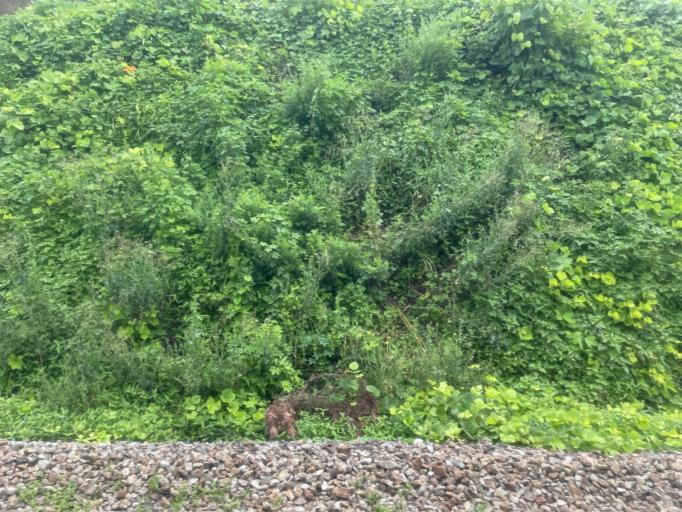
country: JP
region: Gunma
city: Numata
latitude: 36.6829
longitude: 138.9966
